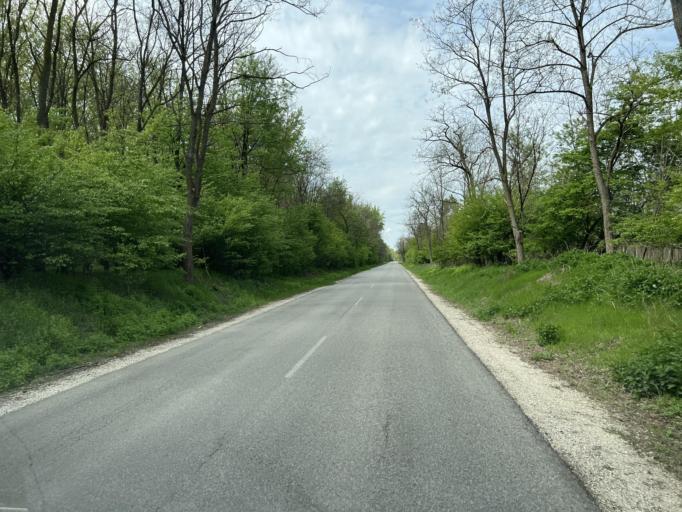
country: HU
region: Pest
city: Csemo
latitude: 47.1527
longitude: 19.6185
